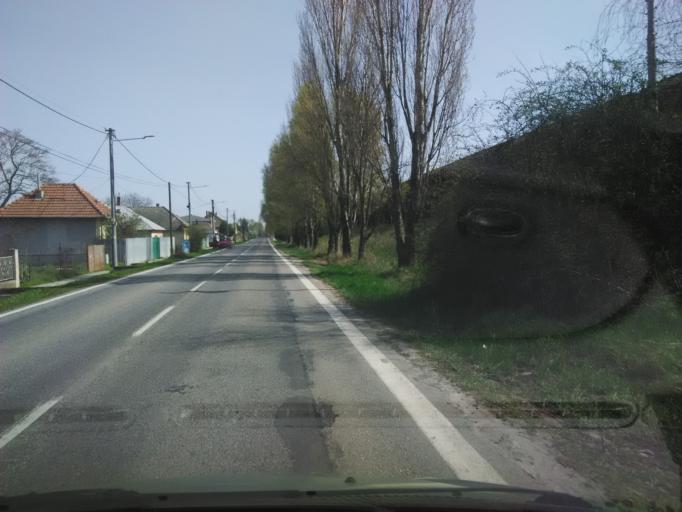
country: SK
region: Nitriansky
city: Sellye
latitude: 48.1523
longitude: 17.9336
